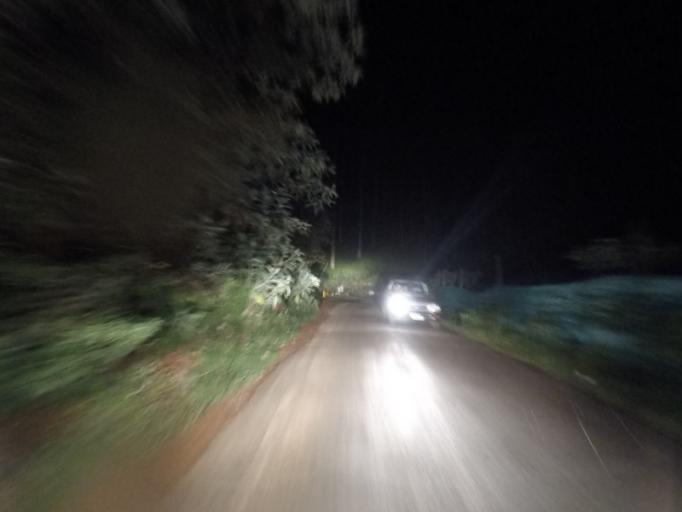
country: IN
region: Tamil Nadu
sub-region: Nilgiri
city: Kotagiri
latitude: 11.4723
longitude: 76.8881
